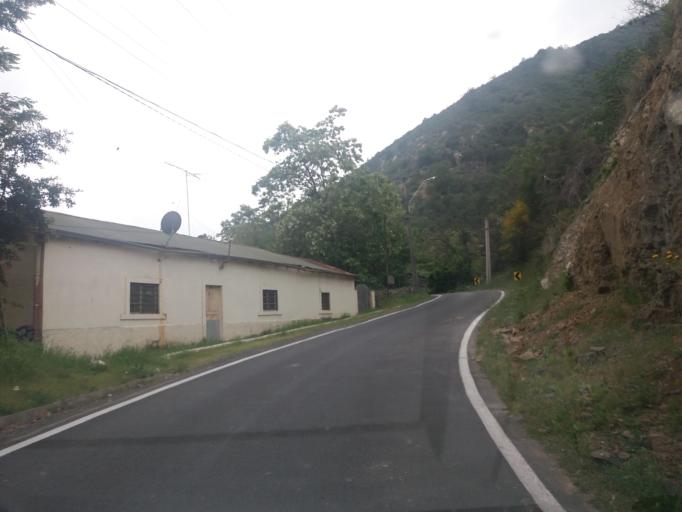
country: CL
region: Valparaiso
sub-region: Provincia de Marga Marga
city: Limache
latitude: -33.0394
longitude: -71.0953
